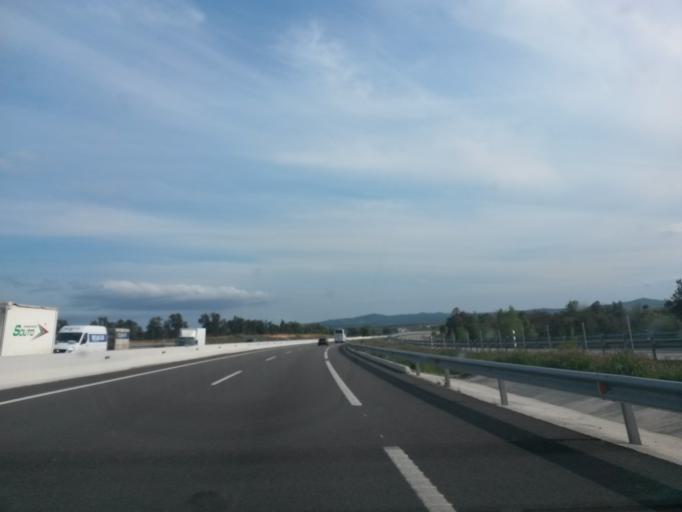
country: ES
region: Catalonia
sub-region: Provincia de Girona
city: Sils
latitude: 41.8266
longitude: 2.7628
